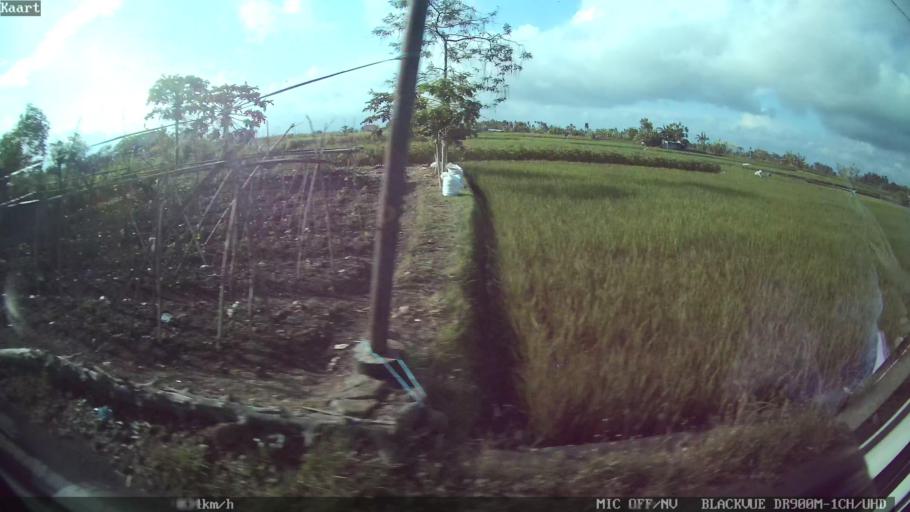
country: ID
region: Bali
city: Banjar Desa
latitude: -8.5796
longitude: 115.2324
